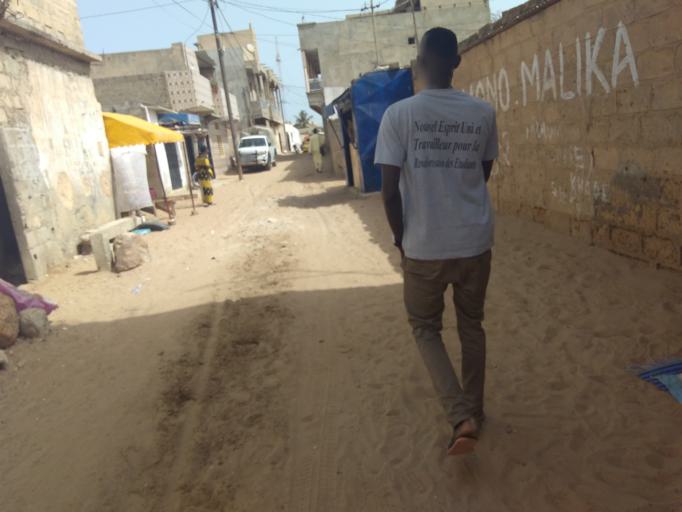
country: SN
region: Dakar
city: Pikine
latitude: 14.7925
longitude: -17.3364
